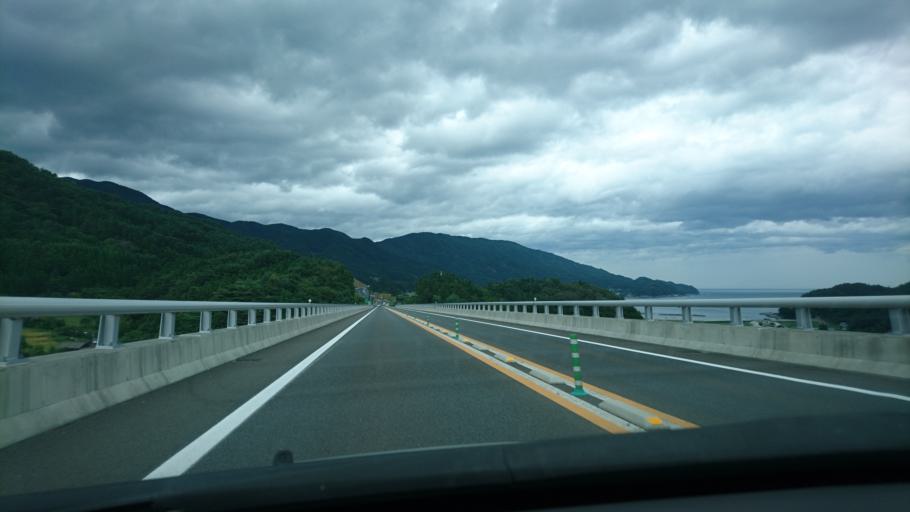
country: JP
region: Iwate
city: Ofunato
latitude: 39.1426
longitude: 141.8205
